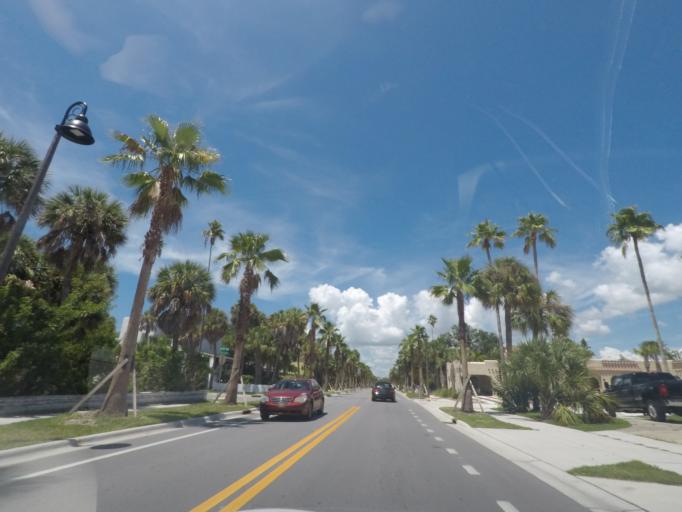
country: US
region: Florida
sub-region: Pinellas County
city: Tierra Verde
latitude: 27.7033
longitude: -82.7362
